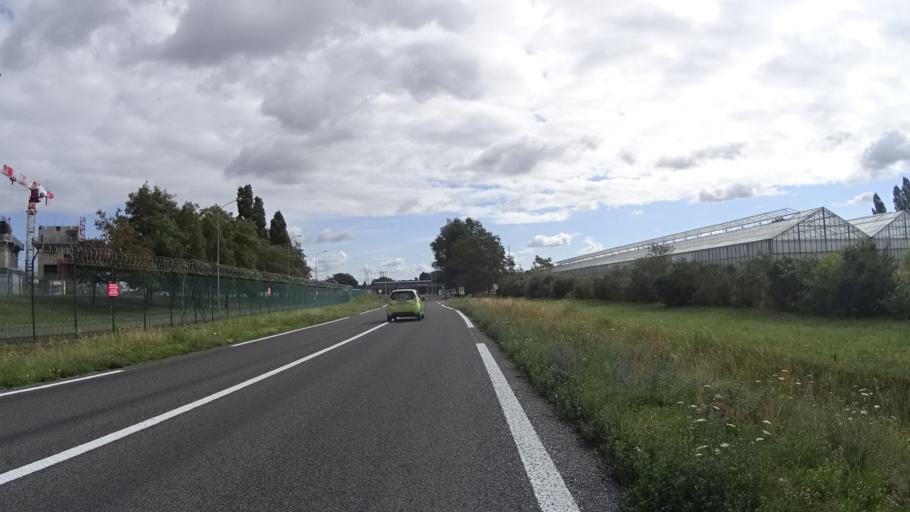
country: FR
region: Centre
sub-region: Departement d'Indre-et-Loire
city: Avoine
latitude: 47.2230
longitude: 0.1706
